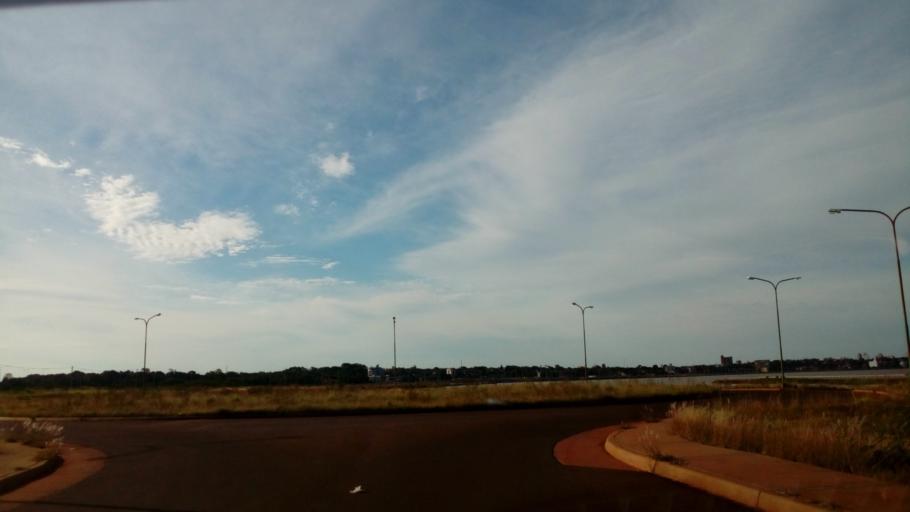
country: AR
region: Misiones
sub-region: Departamento de Capital
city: Posadas
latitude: -27.4127
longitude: -55.8855
